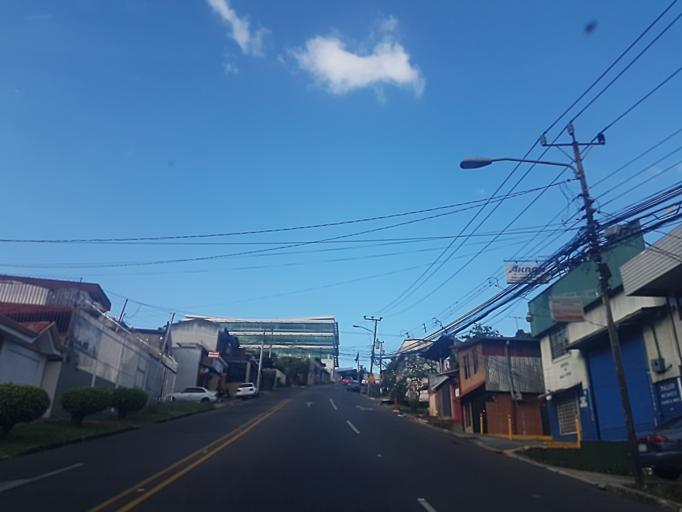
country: CR
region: San Jose
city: San Jose
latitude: 9.9268
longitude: -84.1043
